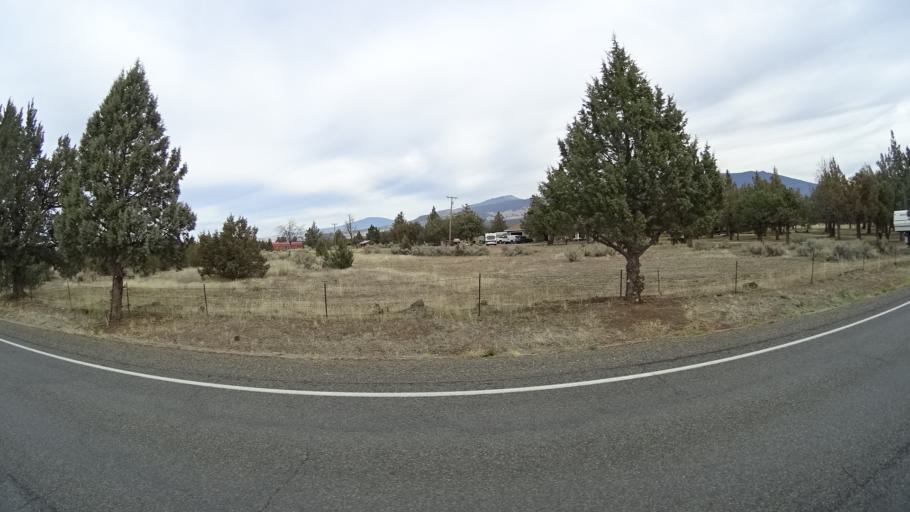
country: US
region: California
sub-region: Siskiyou County
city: Weed
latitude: 41.6015
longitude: -122.3506
